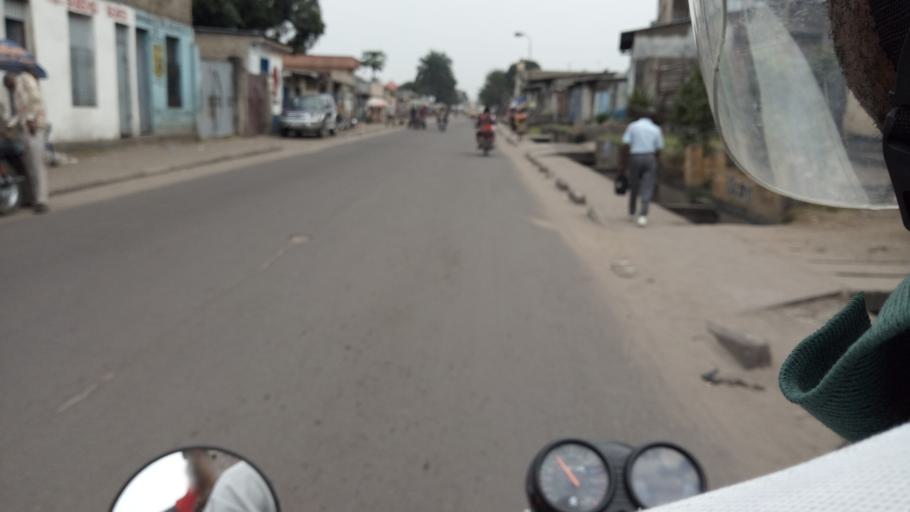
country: CD
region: Kinshasa
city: Kinshasa
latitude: -4.4053
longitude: 15.3163
